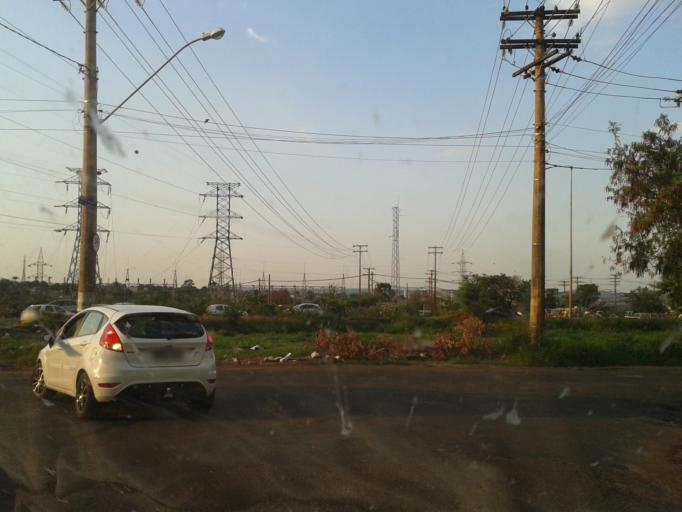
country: BR
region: Minas Gerais
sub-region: Uberlandia
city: Uberlandia
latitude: -18.9099
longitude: -48.3349
